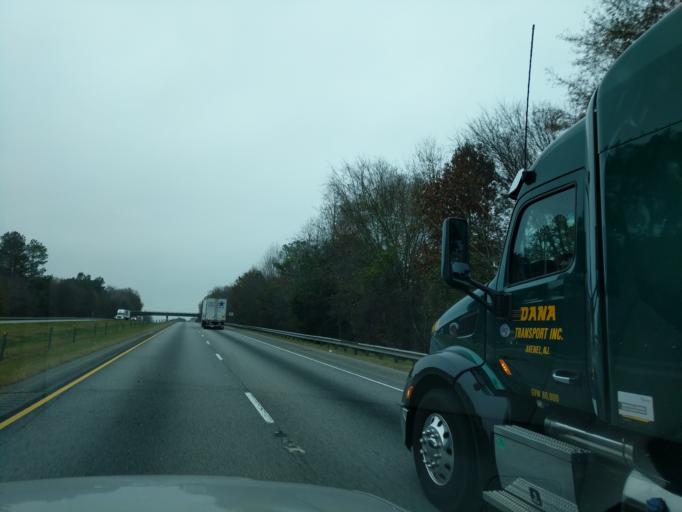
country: US
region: Georgia
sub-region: Franklin County
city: Carnesville
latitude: 34.3680
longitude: -83.2805
